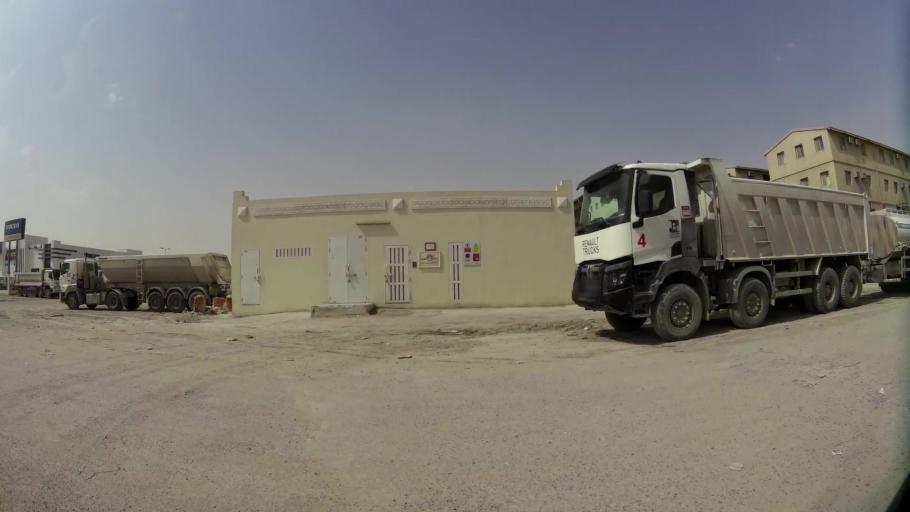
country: QA
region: Al Wakrah
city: Al Wukayr
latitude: 25.1694
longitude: 51.4395
